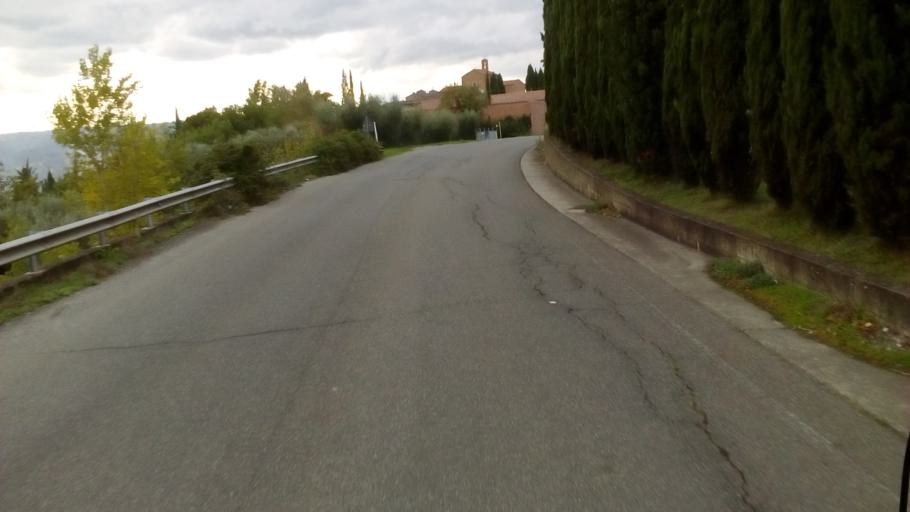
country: IT
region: Tuscany
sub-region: Province of Florence
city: Castelfiorentino
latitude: 43.6138
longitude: 10.9793
